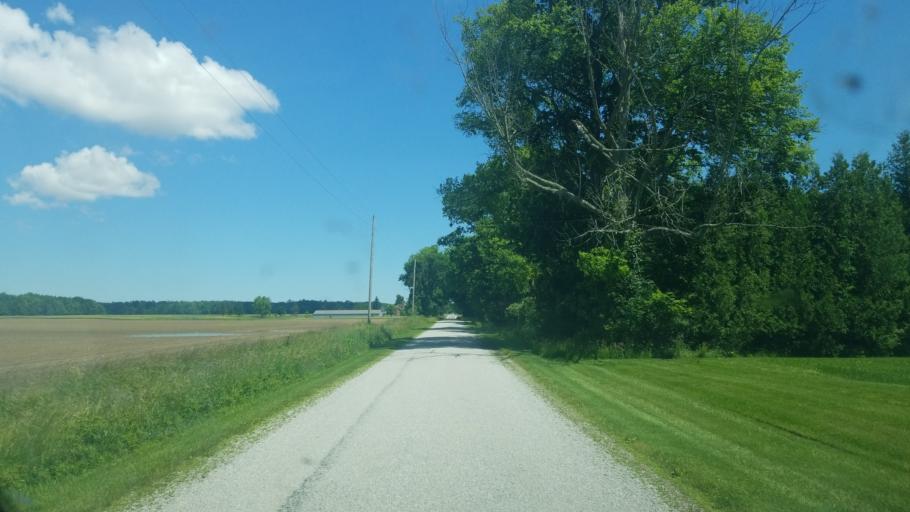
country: US
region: Ohio
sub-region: Huron County
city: New London
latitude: 41.1565
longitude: -82.3896
